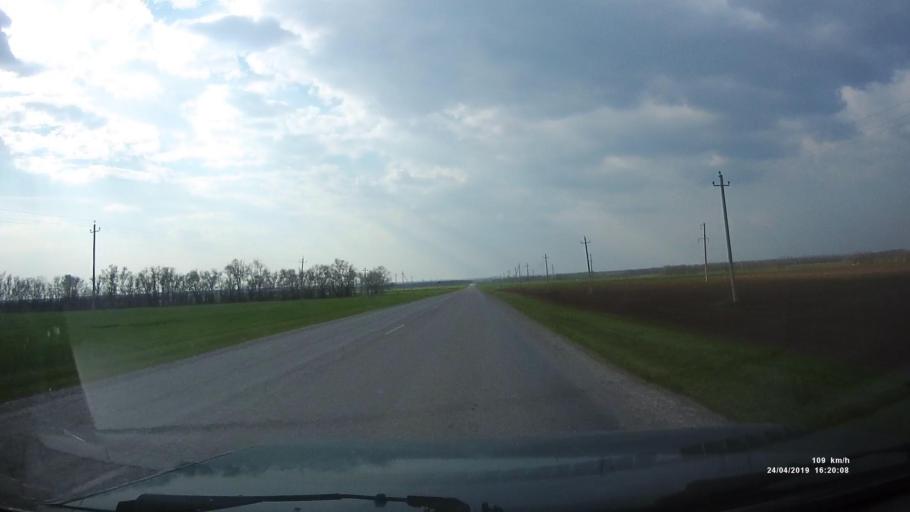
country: RU
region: Rostov
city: Orlovskiy
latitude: 46.7887
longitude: 42.0862
